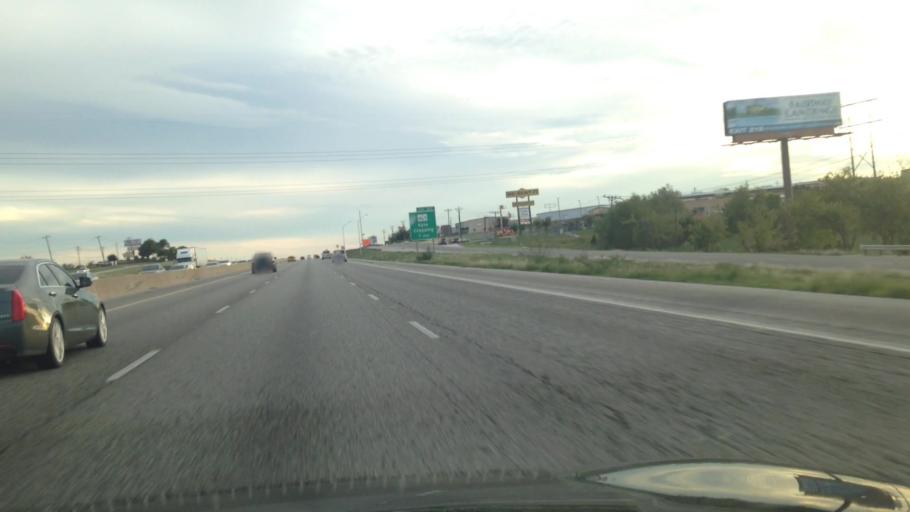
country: US
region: Texas
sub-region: Hays County
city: Buda
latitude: 30.0716
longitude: -97.8279
